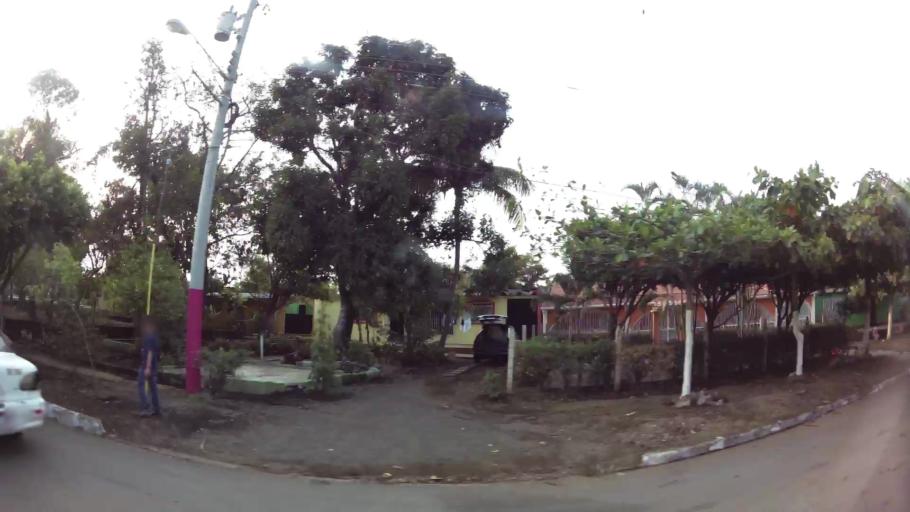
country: NI
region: Masaya
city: Masaya
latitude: 11.9808
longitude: -86.0766
